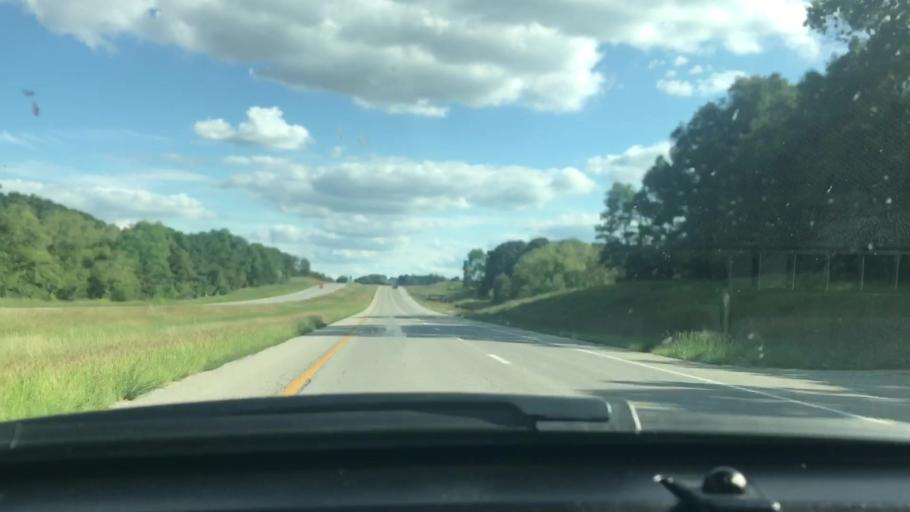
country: US
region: Missouri
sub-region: Howell County
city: West Plains
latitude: 36.8315
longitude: -91.9152
